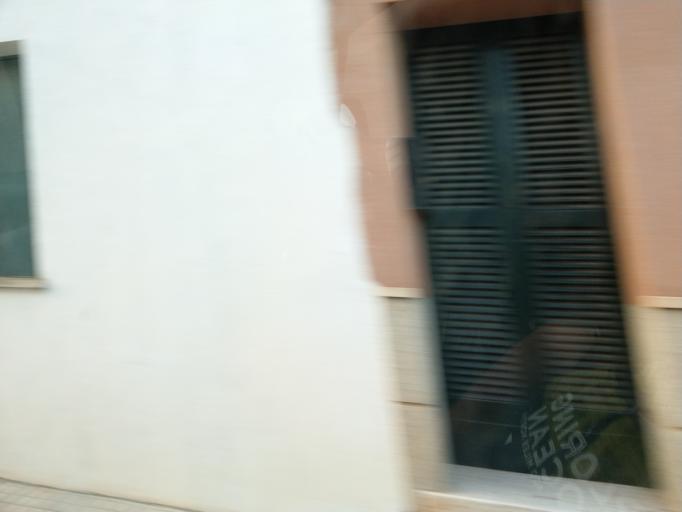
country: ES
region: Balearic Islands
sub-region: Illes Balears
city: Ses Salines
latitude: 39.3409
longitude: 3.0592
